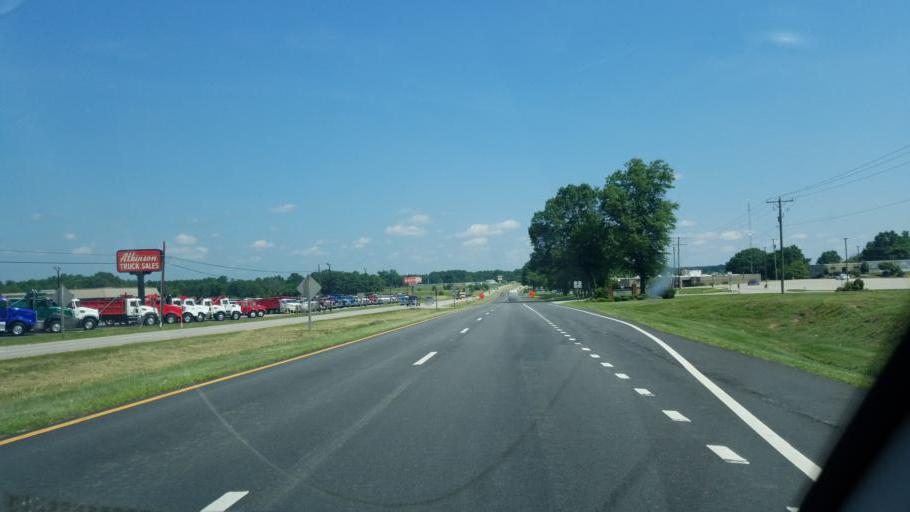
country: US
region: Virginia
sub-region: Pittsylvania County
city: Chatham
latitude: 36.7609
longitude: -79.3894
